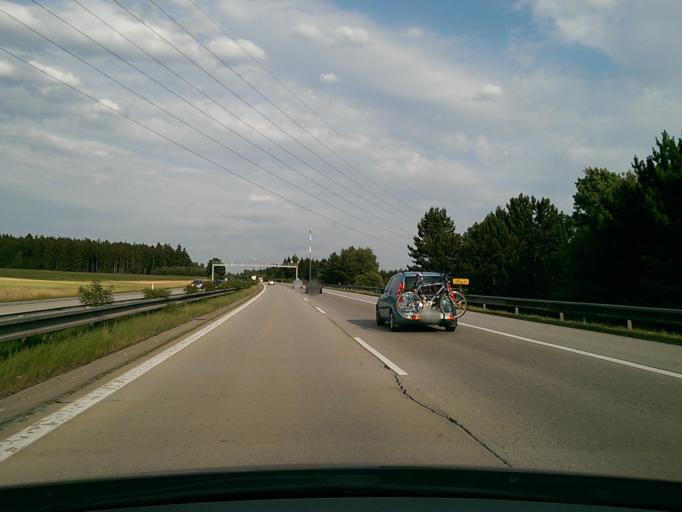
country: CZ
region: Vysocina
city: Velky Beranov
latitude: 49.4268
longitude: 15.6642
